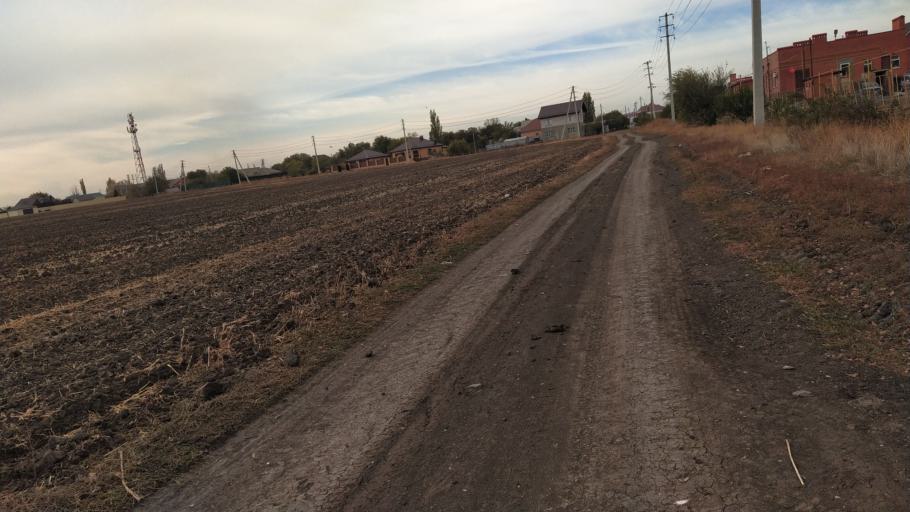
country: RU
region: Rostov
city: Bataysk
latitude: 47.1119
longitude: 39.6802
